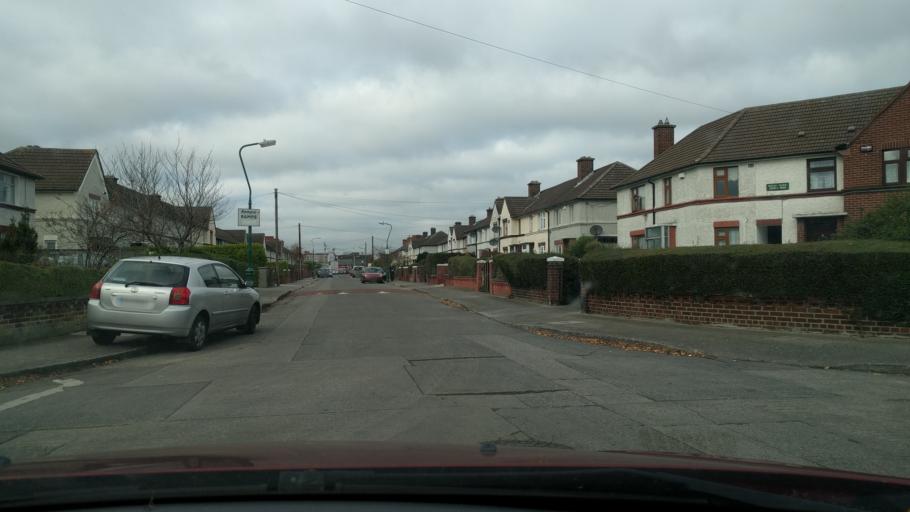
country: IE
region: Leinster
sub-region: South Dublin
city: Terenure
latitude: 53.3136
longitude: -6.2930
